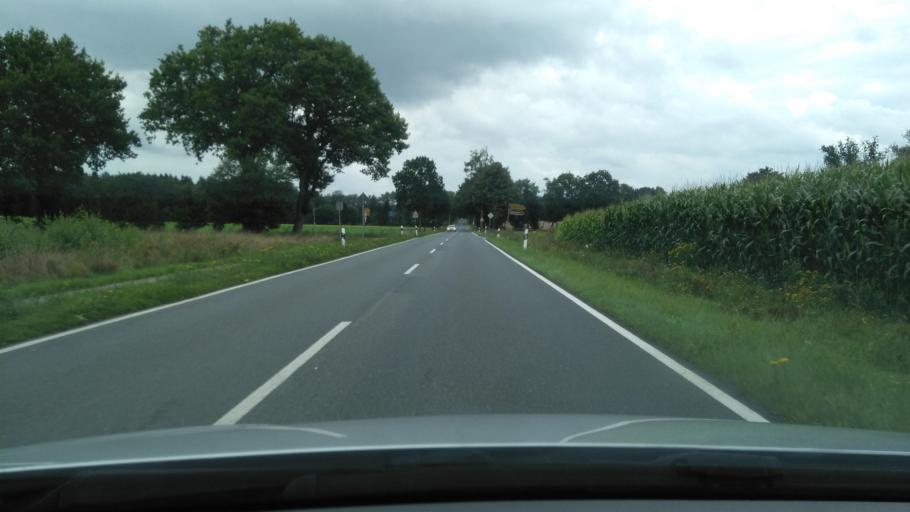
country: DE
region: Lower Saxony
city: Walsrode
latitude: 52.8939
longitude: 9.5745
